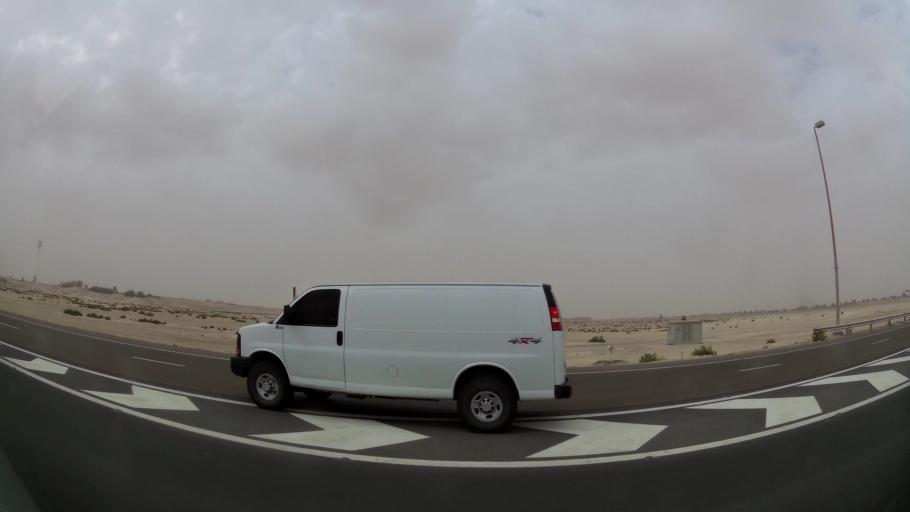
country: AE
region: Abu Dhabi
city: Abu Dhabi
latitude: 24.4082
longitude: 54.7157
